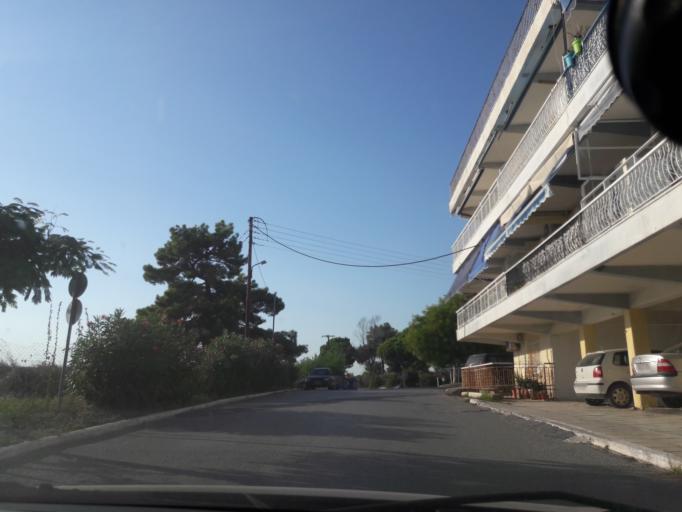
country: GR
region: Central Macedonia
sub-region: Nomos Chalkidikis
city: Nea Kallikrateia
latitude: 40.3460
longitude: 23.0131
